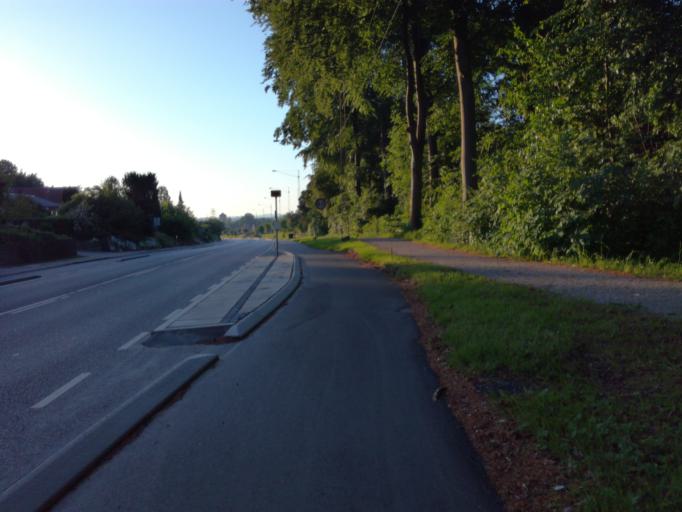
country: DK
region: South Denmark
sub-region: Middelfart Kommune
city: Middelfart
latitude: 55.5012
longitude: 9.7137
